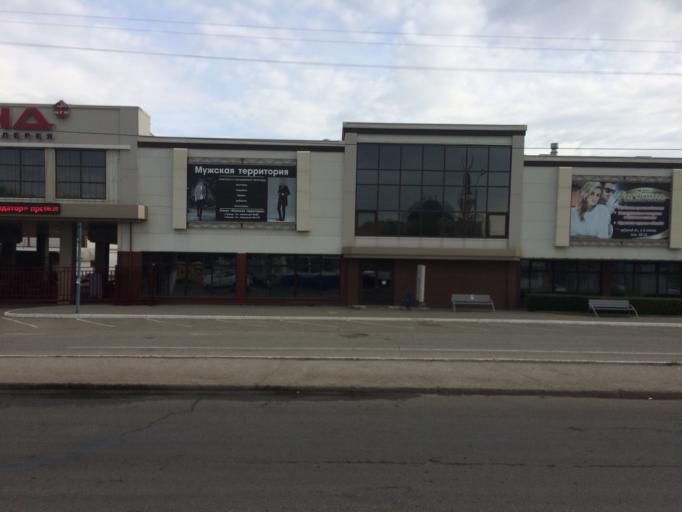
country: RU
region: Chelyabinsk
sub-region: Gorod Magnitogorsk
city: Magnitogorsk
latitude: 53.3980
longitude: 58.9903
